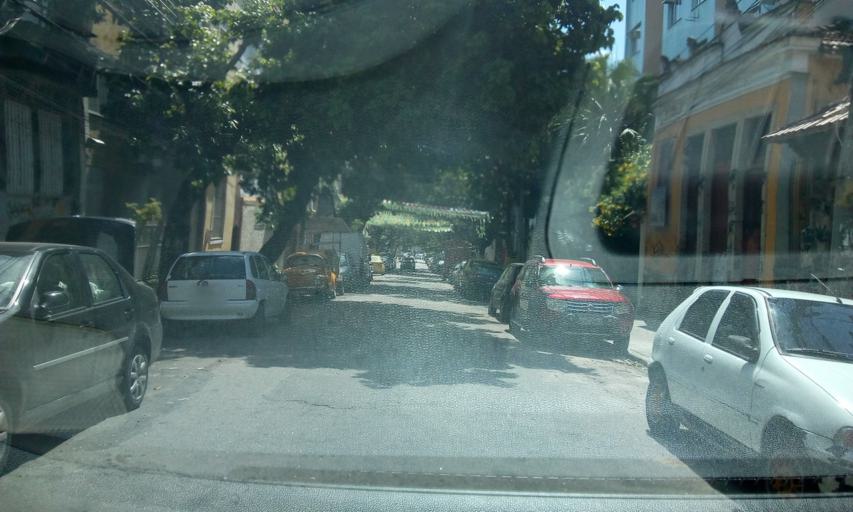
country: BR
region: Rio de Janeiro
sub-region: Rio De Janeiro
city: Rio de Janeiro
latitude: -22.9226
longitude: -43.1813
